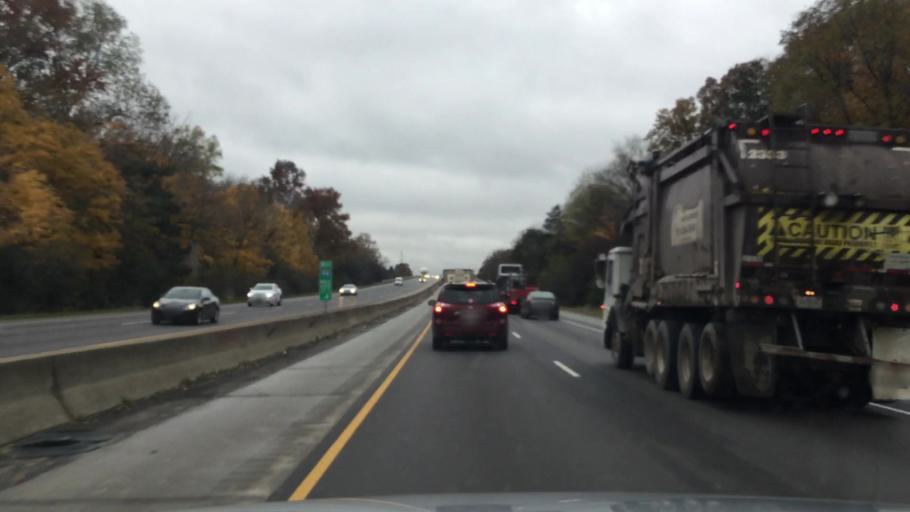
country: US
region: Michigan
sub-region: Washtenaw County
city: Ann Arbor
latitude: 42.2375
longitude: -83.7235
